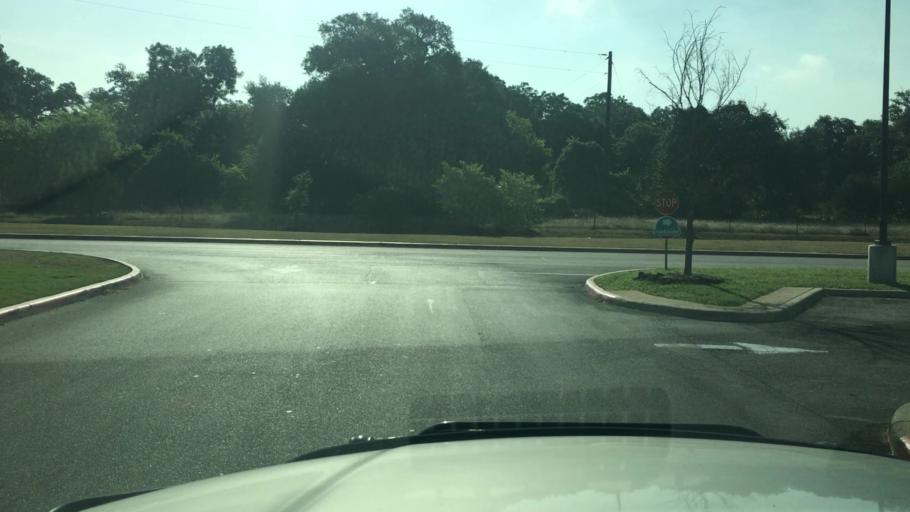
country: US
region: Texas
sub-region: Hays County
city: Dripping Springs
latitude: 30.1907
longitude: -98.0806
